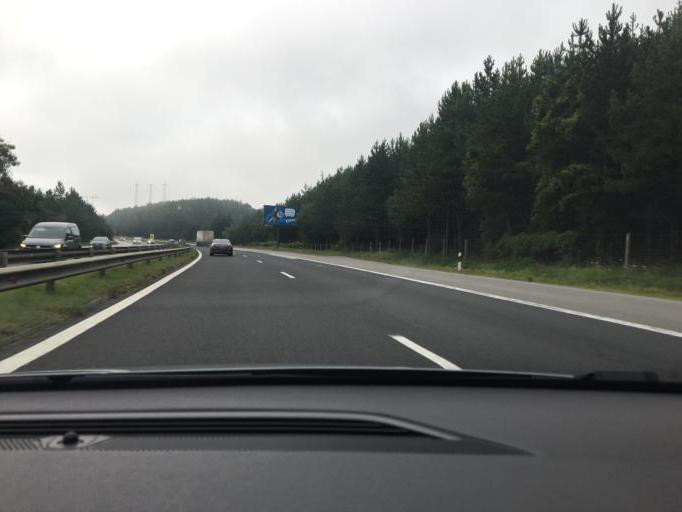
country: BG
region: Sofiya
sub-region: Obshtina Elin Pelin
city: Elin Pelin
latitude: 42.5970
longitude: 23.5716
